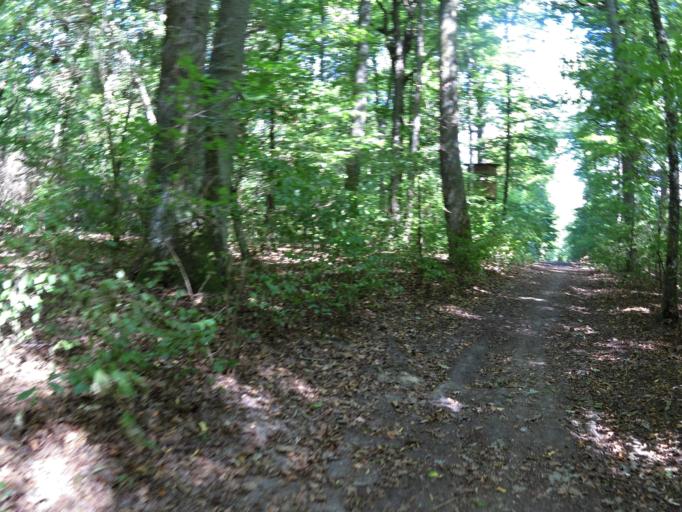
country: DE
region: Bavaria
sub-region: Regierungsbezirk Unterfranken
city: Eisingen
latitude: 49.7672
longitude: 9.8505
